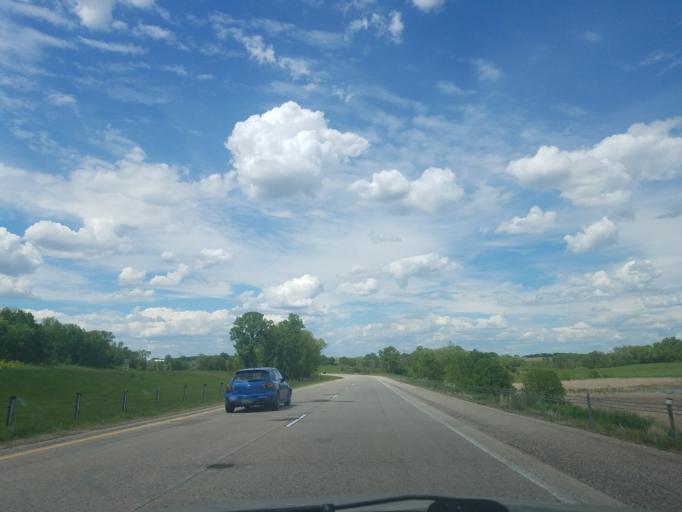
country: US
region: Minnesota
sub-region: Otter Tail County
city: Fergus Falls
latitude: 46.3296
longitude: -96.1226
